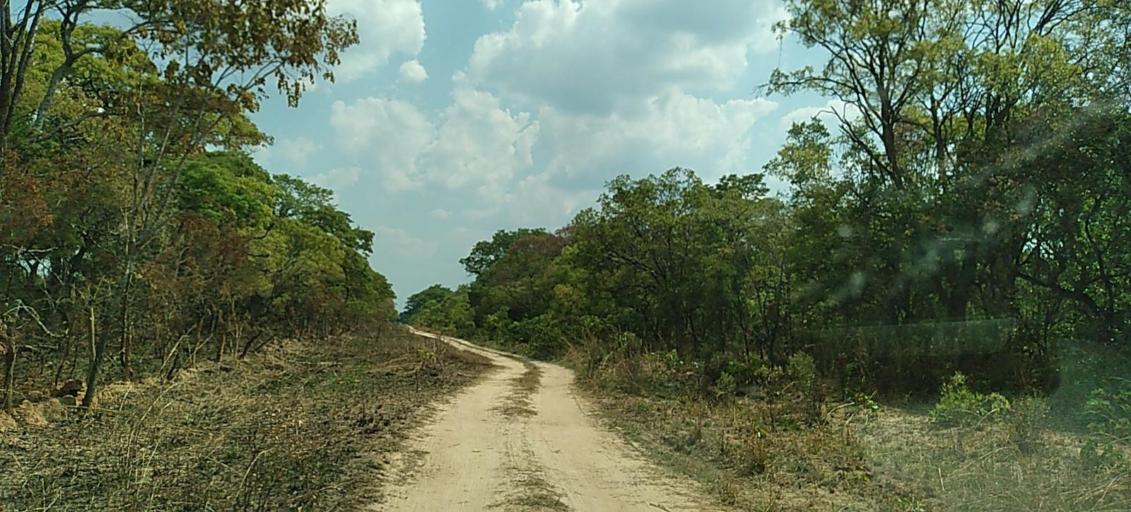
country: ZM
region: Copperbelt
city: Mpongwe
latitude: -13.8398
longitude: 27.9362
